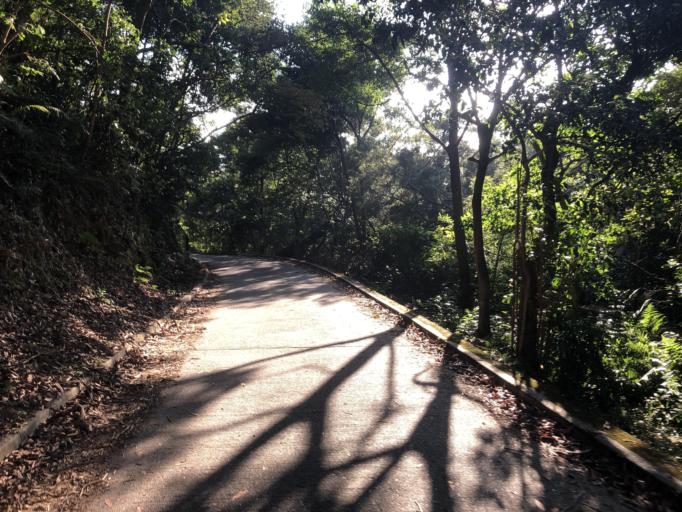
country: HK
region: Tsuen Wan
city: Tsuen Wan
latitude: 22.3955
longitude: 114.0738
